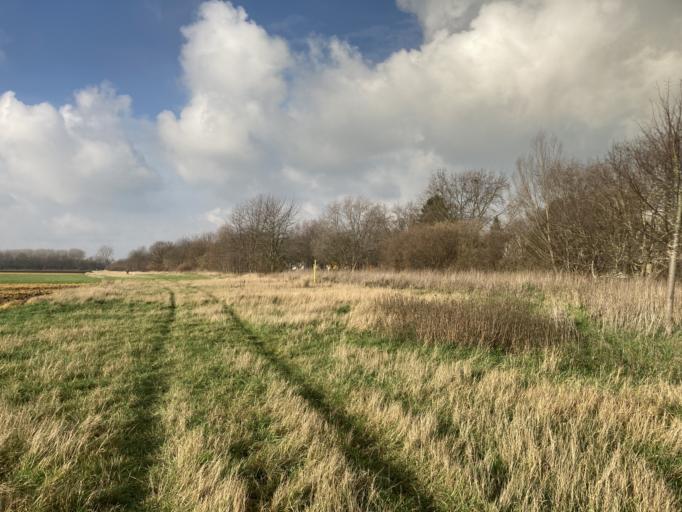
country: DE
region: North Rhine-Westphalia
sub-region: Regierungsbezirk Koln
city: Bergheim
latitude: 50.9291
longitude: 6.6765
